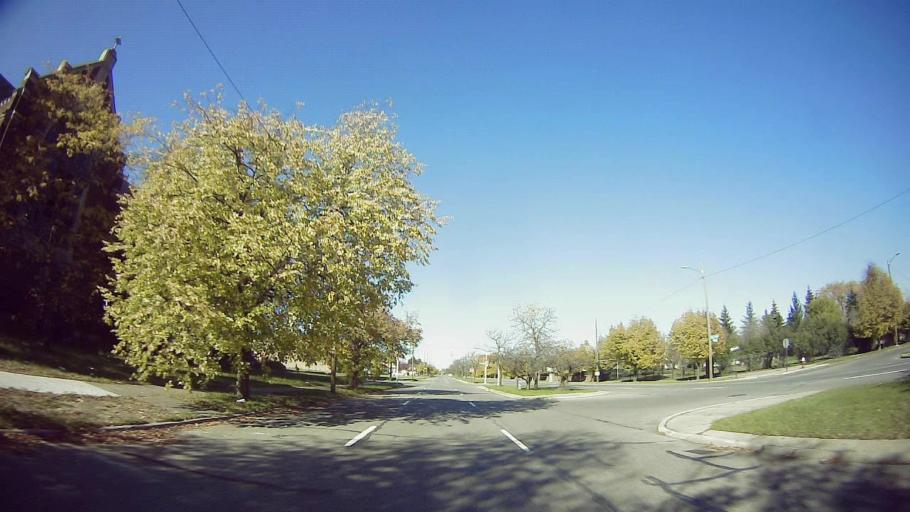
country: US
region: Michigan
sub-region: Wayne County
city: Highland Park
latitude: 42.3667
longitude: -83.0929
